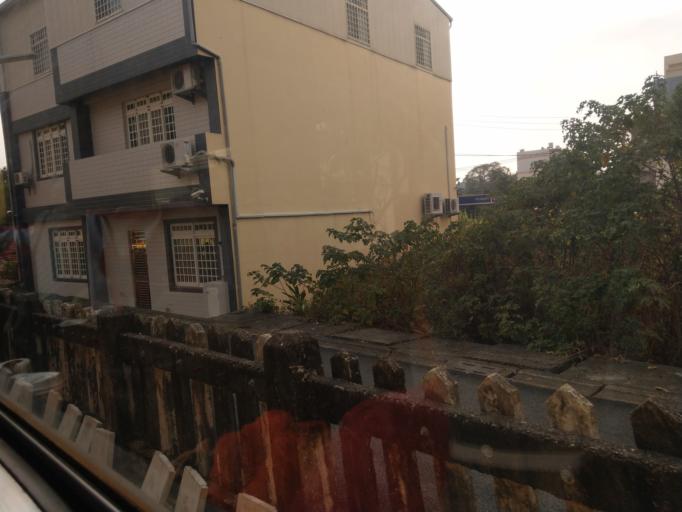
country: TW
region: Taiwan
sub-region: Chiayi
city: Jiayi Shi
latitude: 23.5209
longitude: 120.5490
